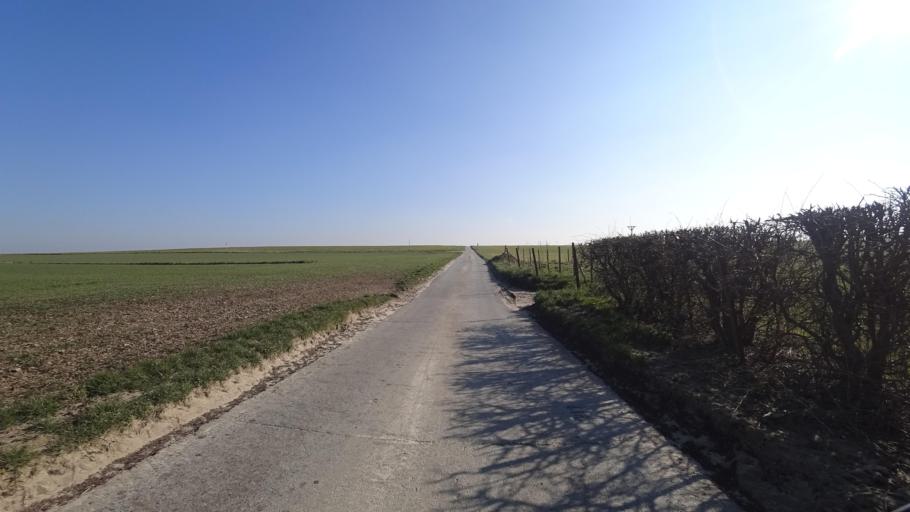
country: BE
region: Wallonia
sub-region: Province du Brabant Wallon
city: Chastre
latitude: 50.5888
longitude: 4.6160
